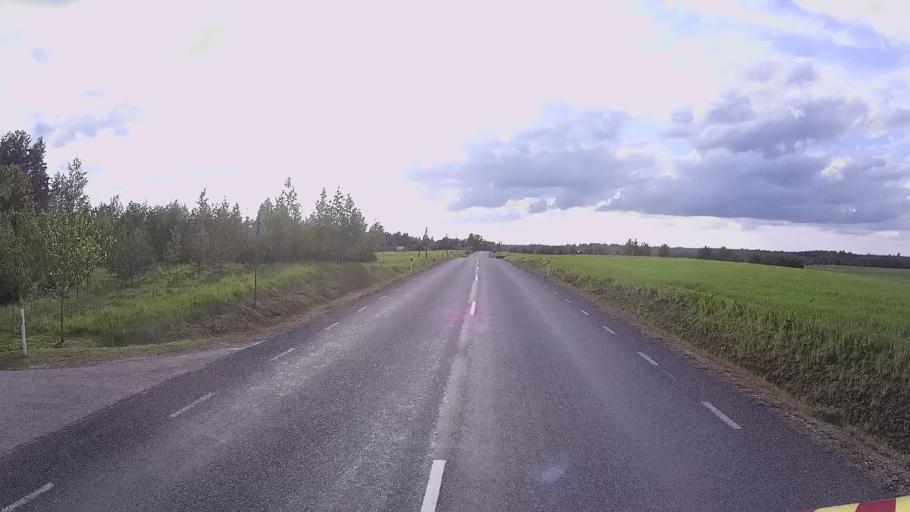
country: EE
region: Jogevamaa
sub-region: Mustvee linn
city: Mustvee
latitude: 59.0443
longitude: 27.0541
